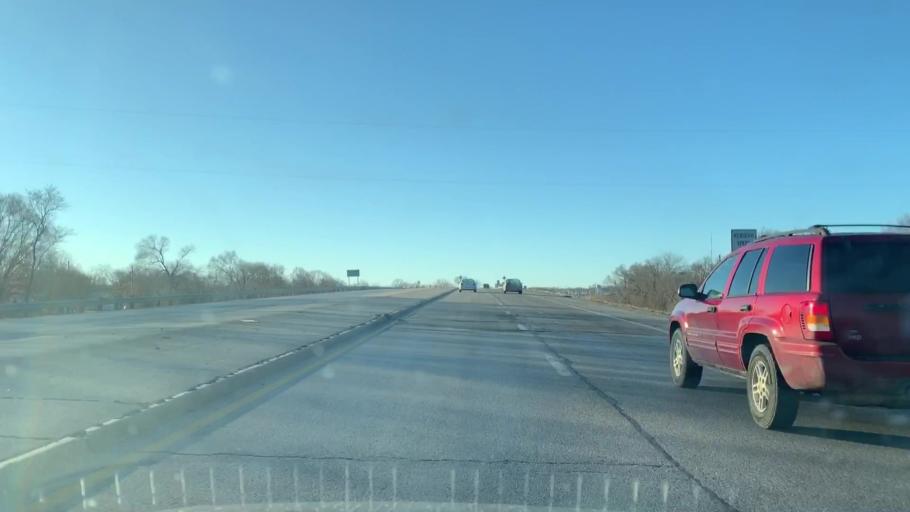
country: US
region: Kansas
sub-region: Bourbon County
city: Fort Scott
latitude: 37.8234
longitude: -94.7043
